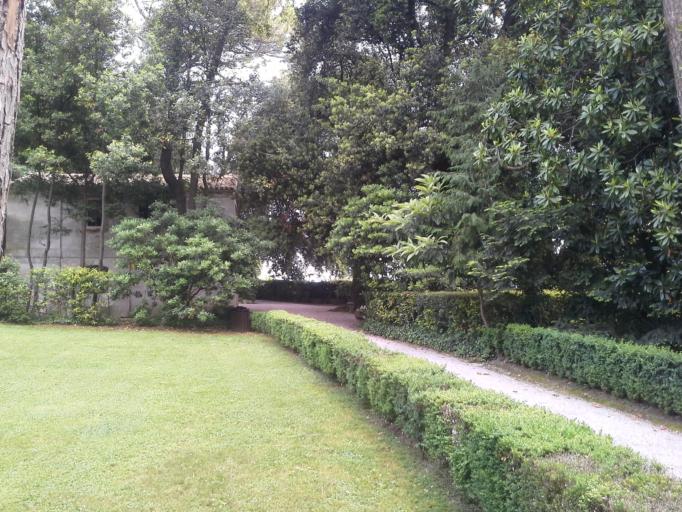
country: IT
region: Lombardy
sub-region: Provincia di Brescia
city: San Felice del Benaco
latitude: 45.5929
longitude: 10.5897
